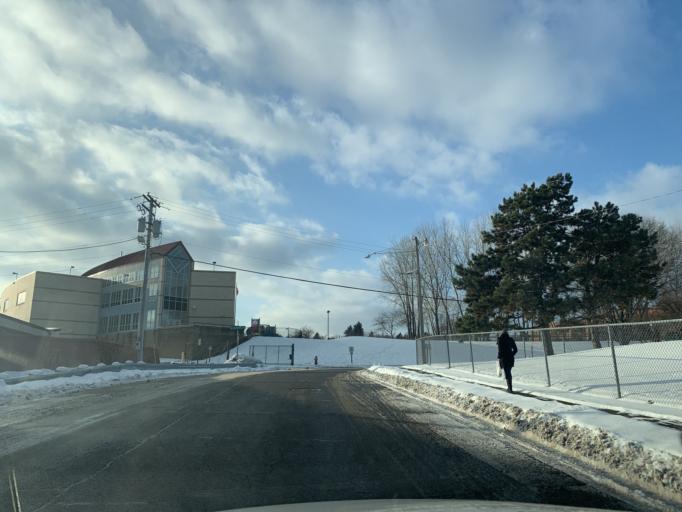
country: US
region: Minnesota
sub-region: Hennepin County
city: Minneapolis
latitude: 44.9816
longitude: -93.2977
